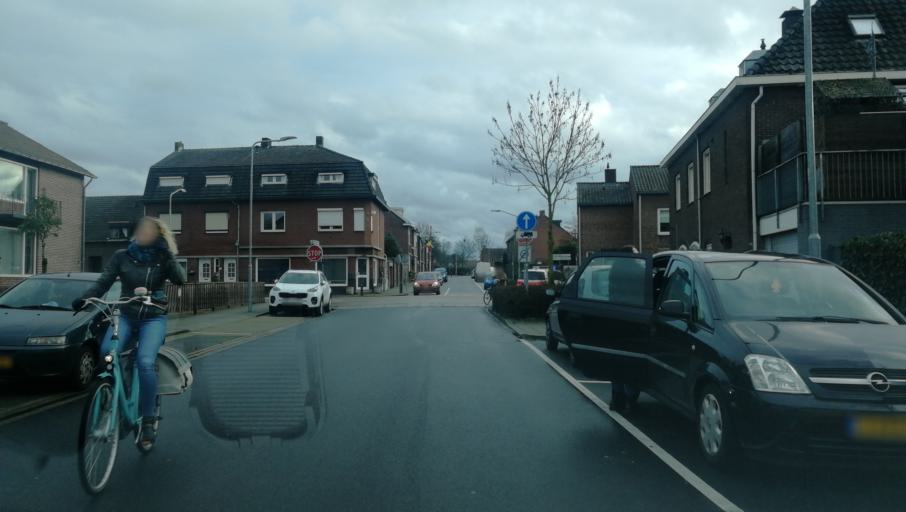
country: NL
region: Limburg
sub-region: Gemeente Venlo
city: Tegelen
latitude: 51.3392
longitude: 6.1393
